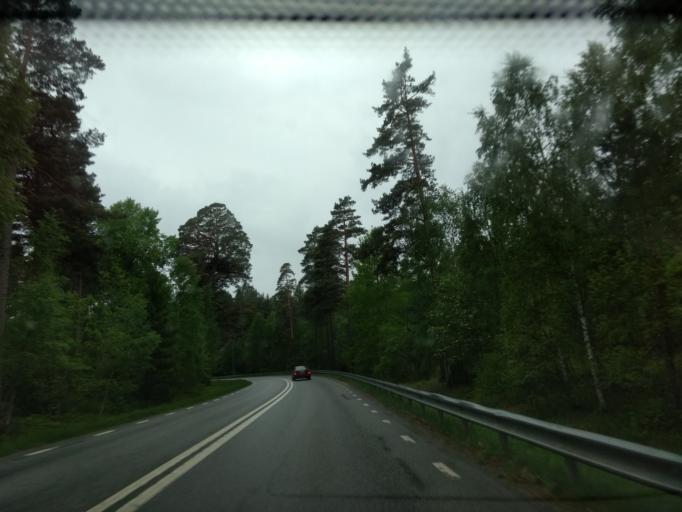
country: SE
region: Uppsala
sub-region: Uppsala Kommun
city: Saevja
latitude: 59.7736
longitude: 17.6586
